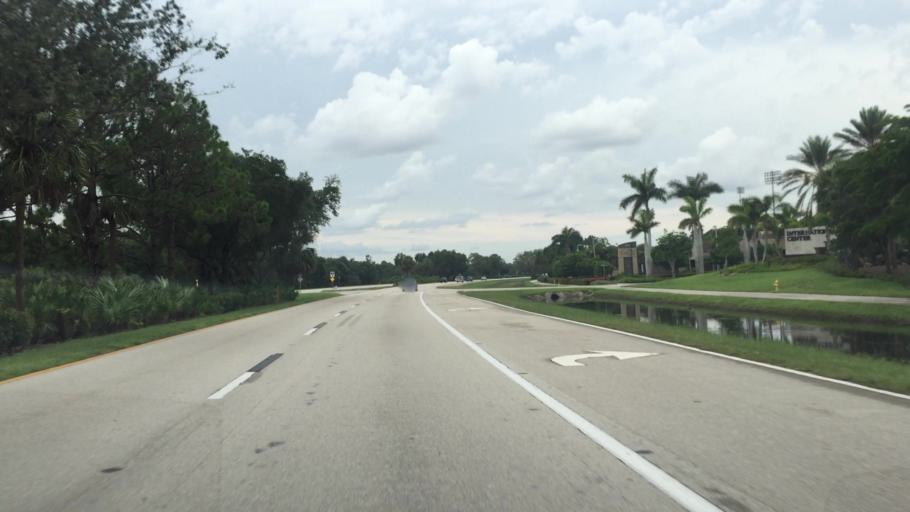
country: US
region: Florida
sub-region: Lee County
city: Villas
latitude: 26.5409
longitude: -81.8397
